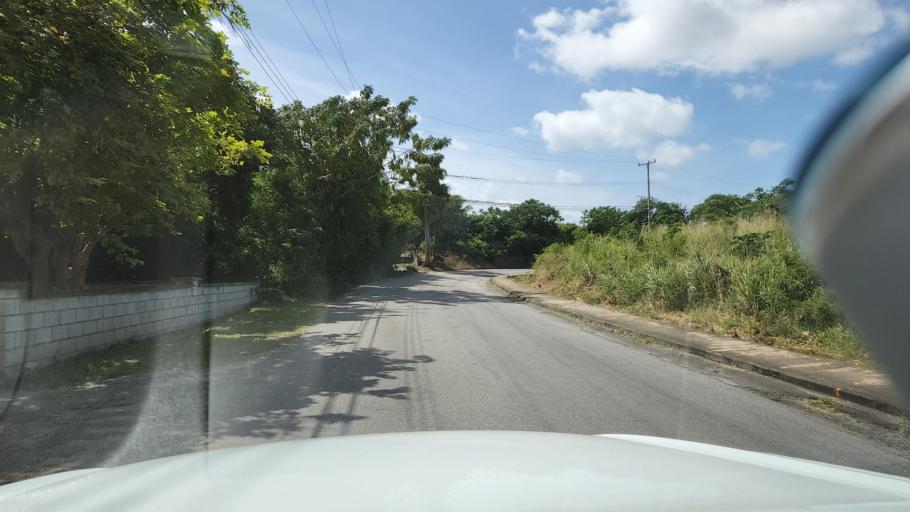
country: BB
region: Christ Church
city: Oistins
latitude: 13.0963
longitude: -59.5570
